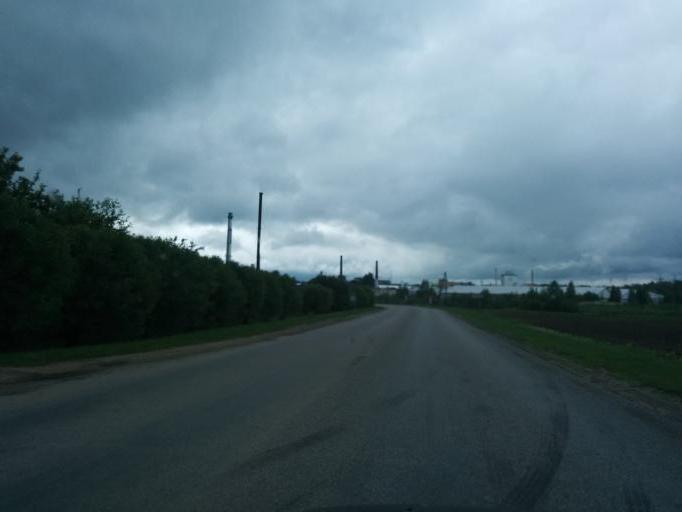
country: LV
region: Valmieras Rajons
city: Valmiera
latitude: 57.5174
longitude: 25.4554
